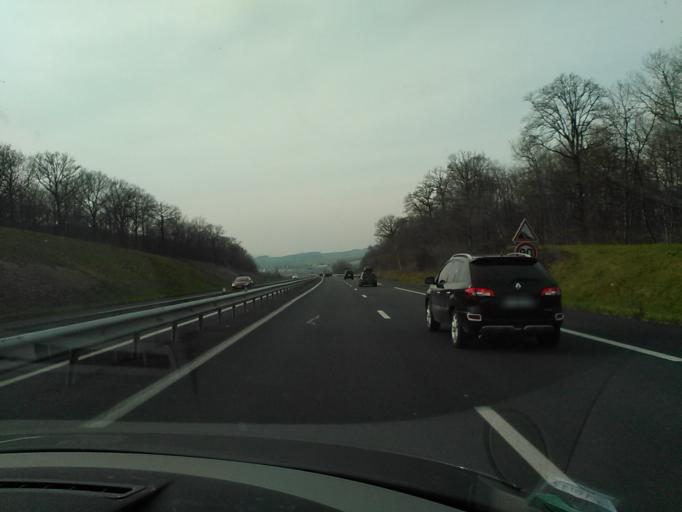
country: FR
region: Bourgogne
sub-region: Departement de l'Yonne
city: Soucy
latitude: 48.2413
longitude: 3.3662
